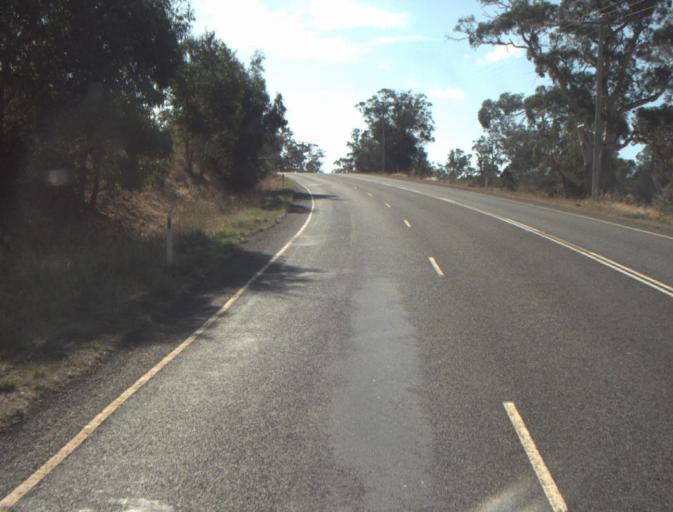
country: AU
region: Tasmania
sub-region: Launceston
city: Mayfield
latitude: -41.3471
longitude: 147.0955
